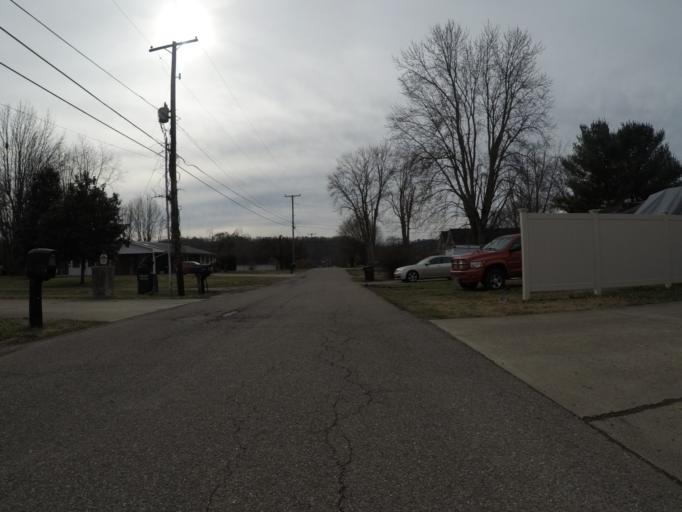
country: US
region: West Virginia
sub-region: Cabell County
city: Pea Ridge
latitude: 38.4463
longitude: -82.3533
